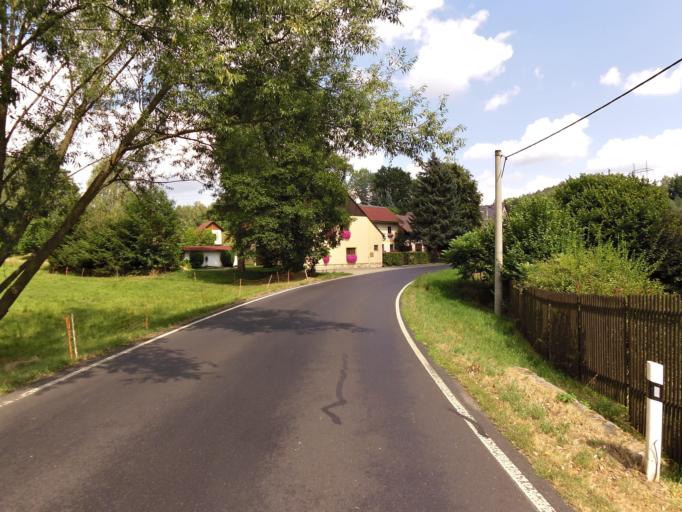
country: CZ
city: Osecna
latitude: 50.7120
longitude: 14.8739
